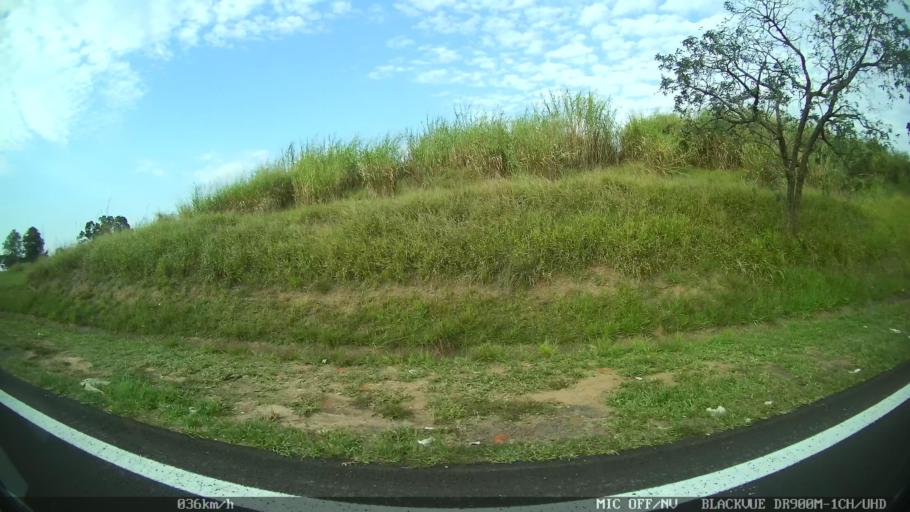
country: BR
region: Sao Paulo
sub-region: Cosmopolis
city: Cosmopolis
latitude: -22.6338
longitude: -47.2077
